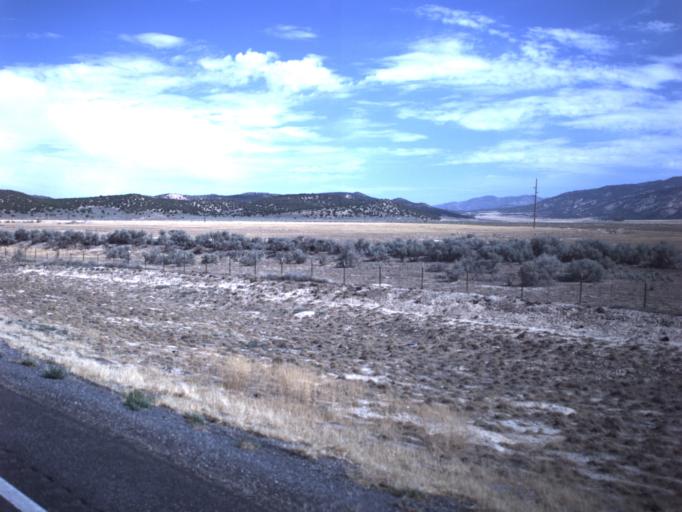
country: US
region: Utah
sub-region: Sanpete County
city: Gunnison
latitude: 39.3142
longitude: -111.9027
